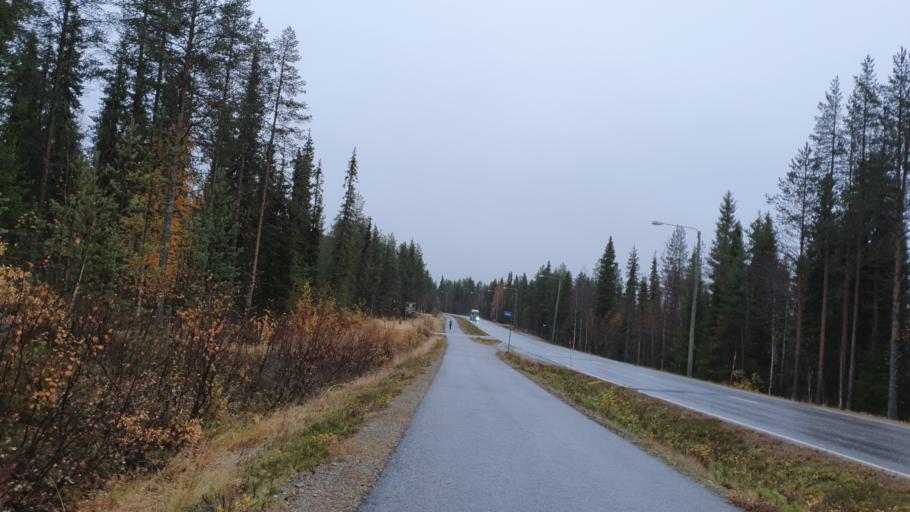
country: FI
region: Lapland
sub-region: Tunturi-Lappi
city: Kolari
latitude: 67.6019
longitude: 24.1304
